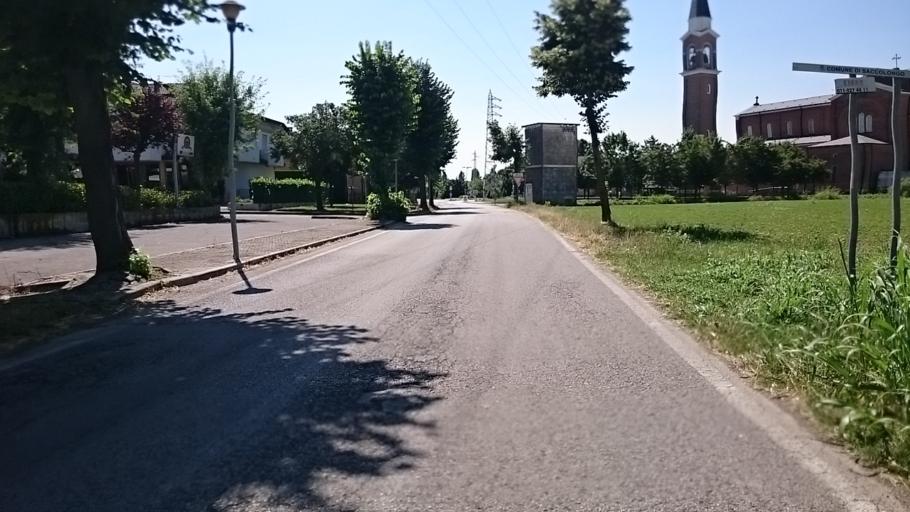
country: IT
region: Veneto
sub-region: Provincia di Padova
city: Saccolongo
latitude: 45.4143
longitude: 11.7399
